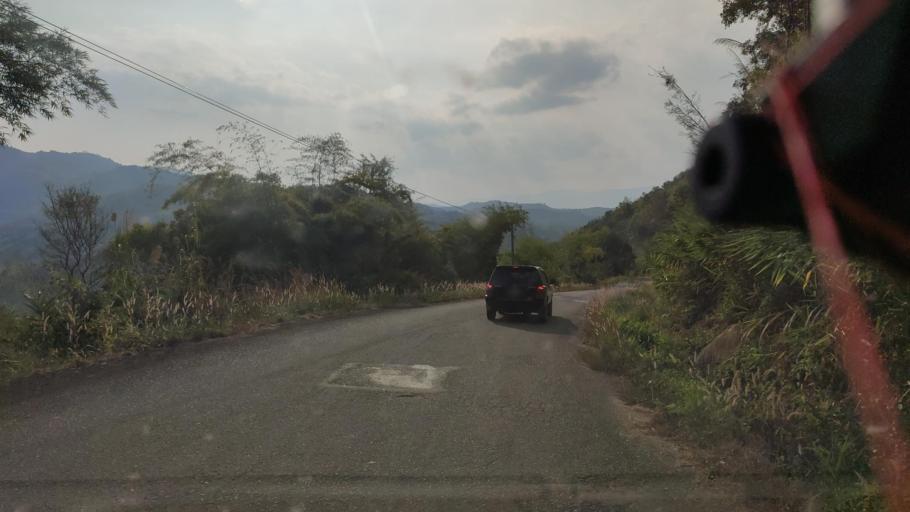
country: CN
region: Yunnan
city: Menghai
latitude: 21.4850
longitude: 99.7247
